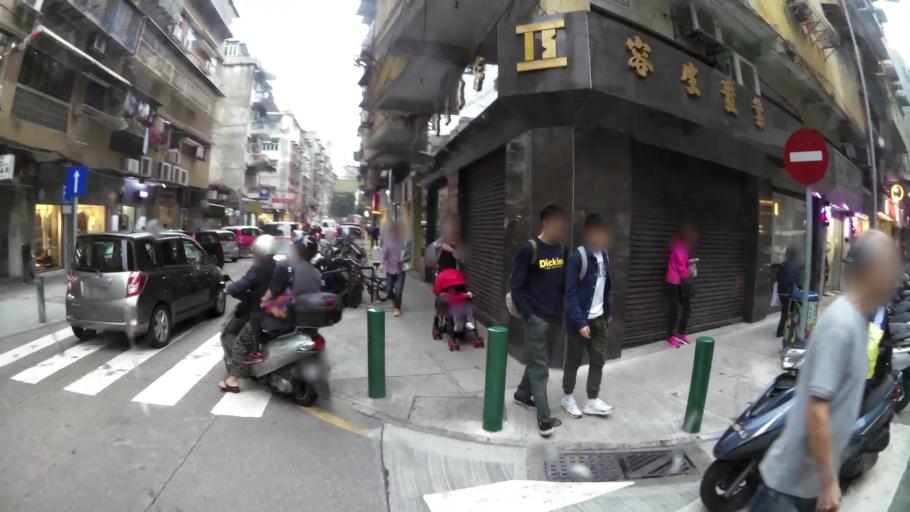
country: MO
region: Macau
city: Macau
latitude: 22.2015
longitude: 113.5460
